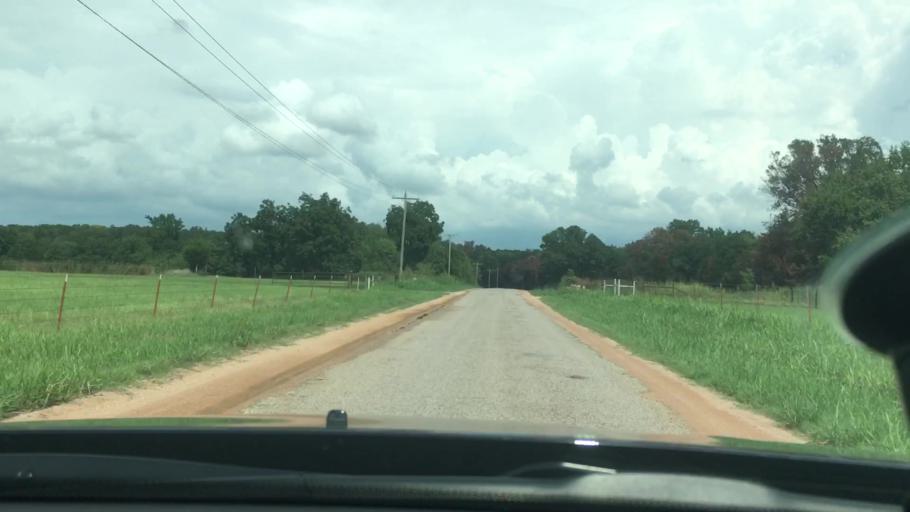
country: US
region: Oklahoma
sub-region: Carter County
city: Dickson
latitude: 34.2374
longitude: -96.9157
